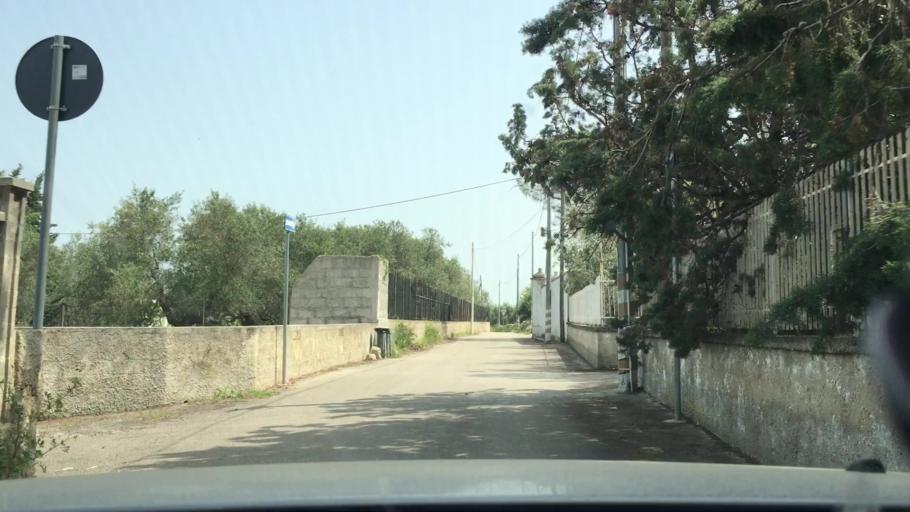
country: IT
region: Apulia
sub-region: Provincia di Barletta - Andria - Trani
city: Capirro
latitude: 41.2547
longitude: 16.4581
